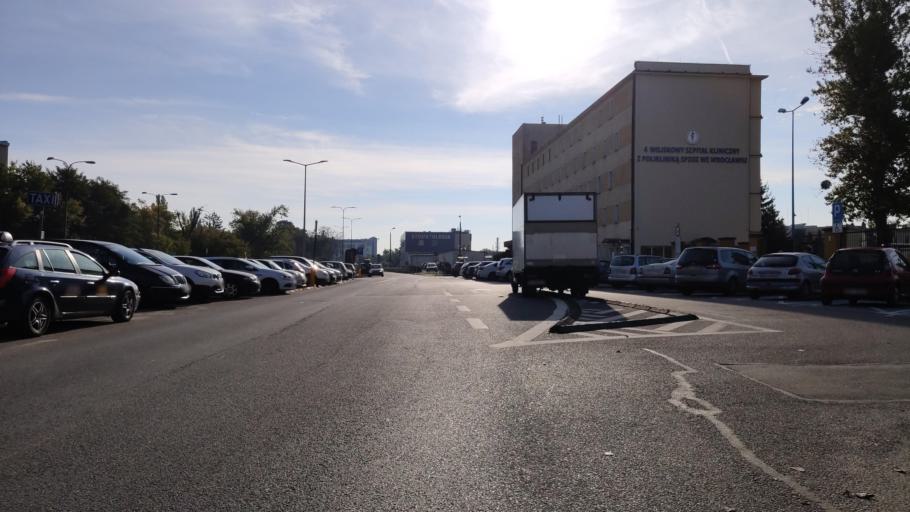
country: PL
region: Lower Silesian Voivodeship
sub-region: Powiat wroclawski
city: Wroclaw
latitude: 51.0761
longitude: 17.0210
